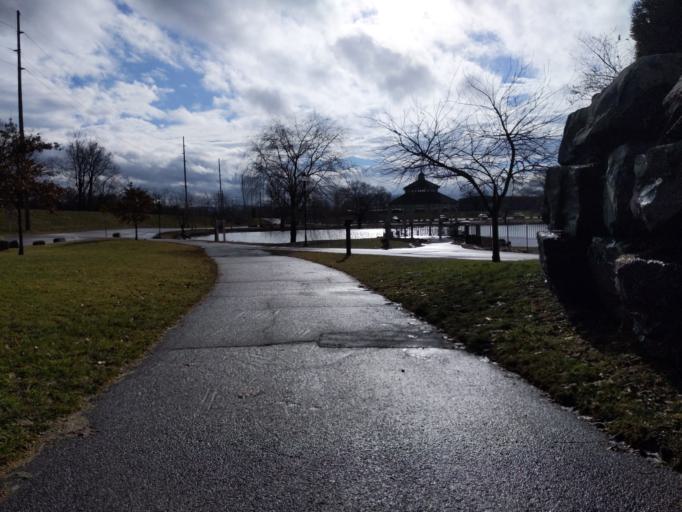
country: US
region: New York
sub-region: Chemung County
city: Elmira Heights
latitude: 42.1144
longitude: -76.8157
